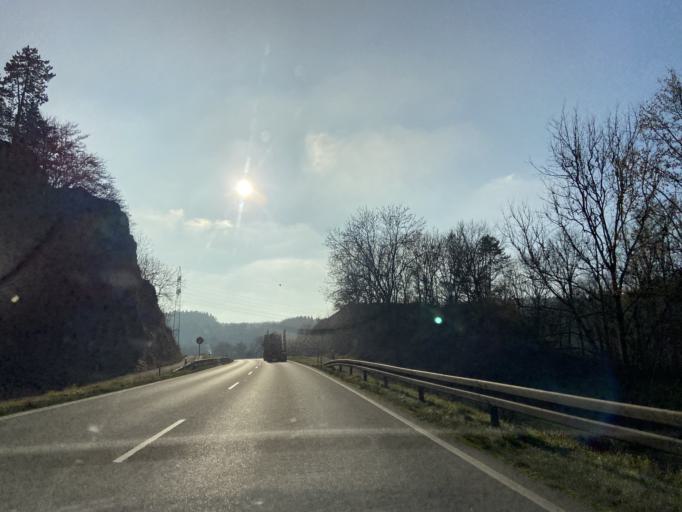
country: DE
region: Baden-Wuerttemberg
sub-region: Tuebingen Region
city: Veringenstadt
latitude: 48.1639
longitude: 9.2011
